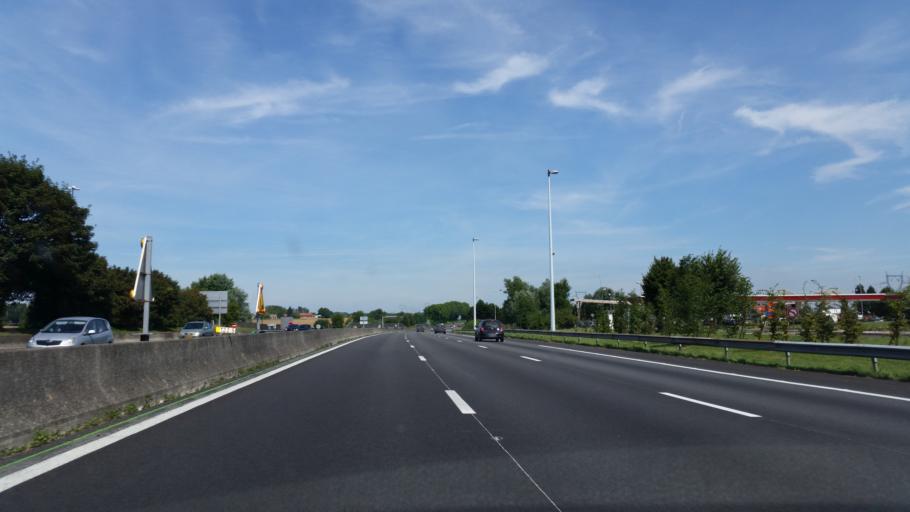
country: FR
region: Picardie
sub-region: Departement de la Somme
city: Chaulnes
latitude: 49.8877
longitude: 2.8390
